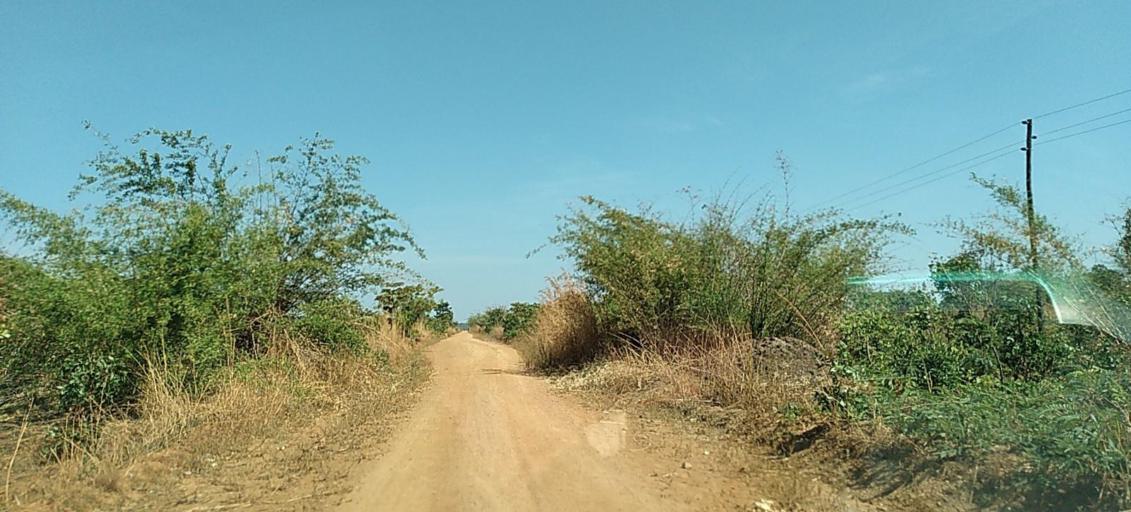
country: ZM
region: Copperbelt
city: Chililabombwe
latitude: -12.3462
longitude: 27.8764
